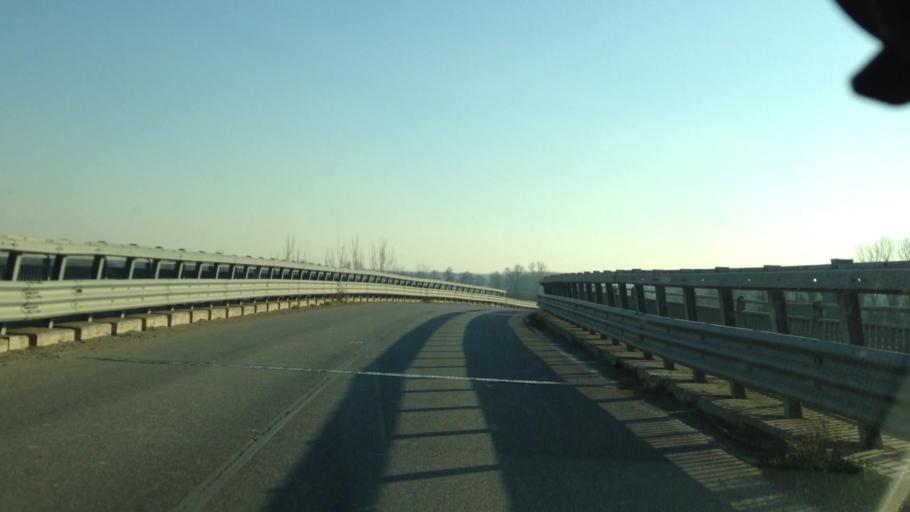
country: IT
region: Piedmont
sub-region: Provincia di Alessandria
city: Felizzano
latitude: 44.8974
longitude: 8.4504
